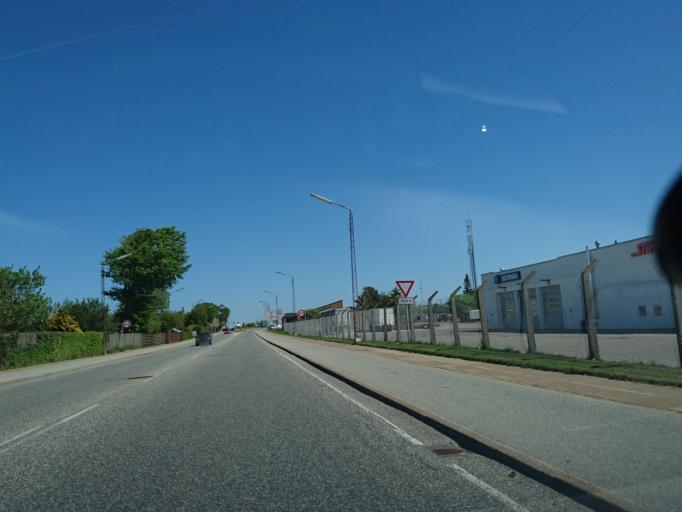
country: DK
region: North Denmark
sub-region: Hjorring Kommune
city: Hjorring
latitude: 57.4472
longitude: 10.0068
